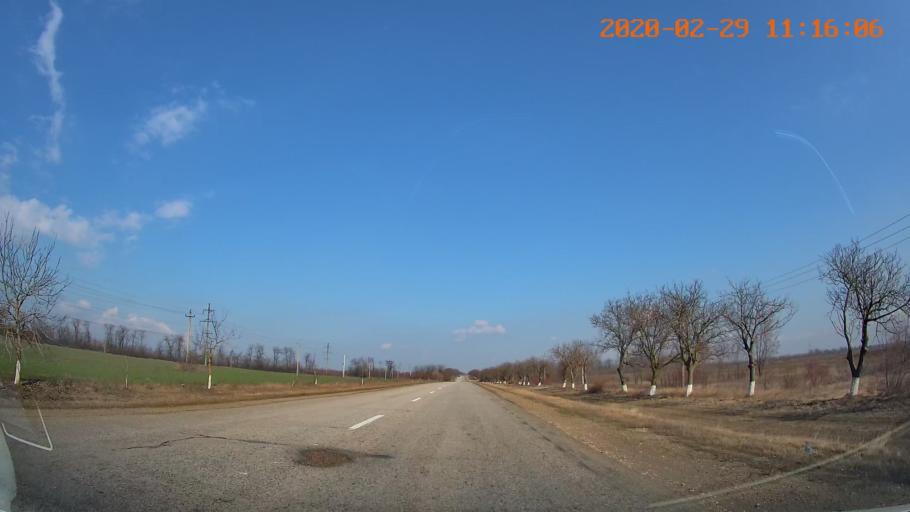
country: MD
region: Telenesti
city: Dubasari
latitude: 47.3039
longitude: 29.1669
